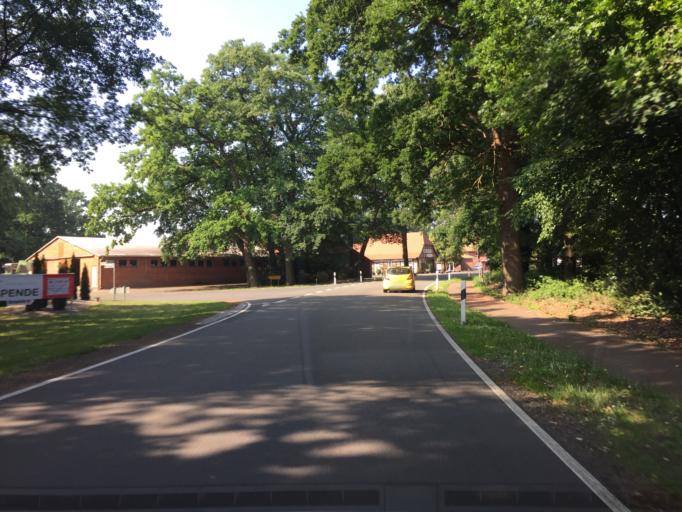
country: DE
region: Lower Saxony
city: Bahrenborstel
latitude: 52.5728
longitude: 8.8167
